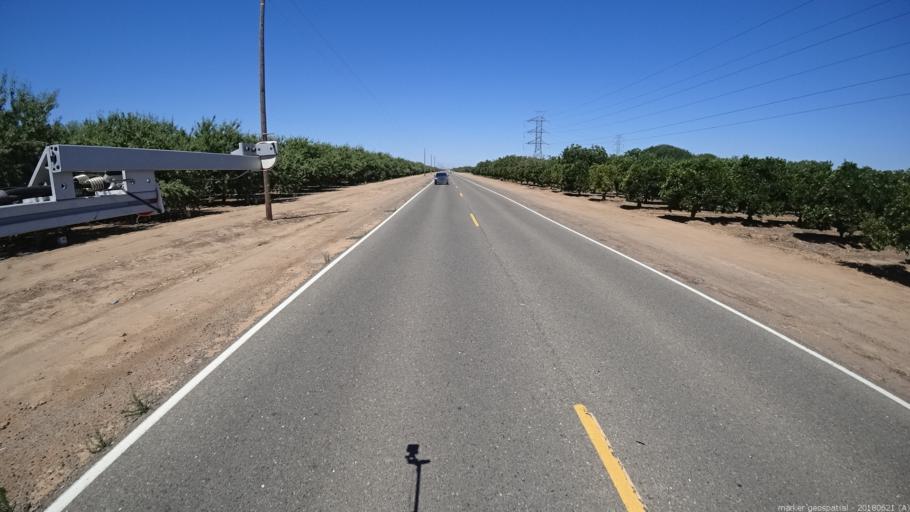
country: US
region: California
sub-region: Fresno County
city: Biola
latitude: 36.8514
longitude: -119.9184
